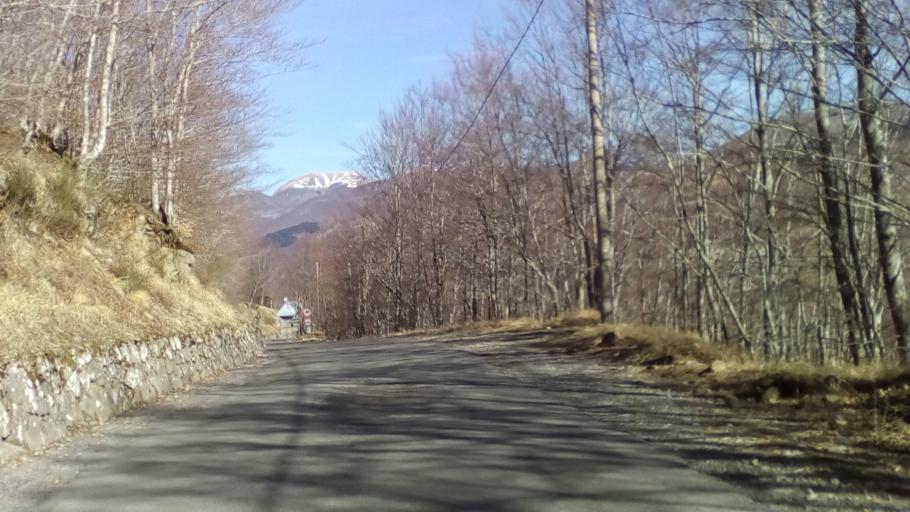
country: IT
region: Tuscany
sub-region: Provincia di Lucca
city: Castiglione di Garfagnana
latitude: 44.1756
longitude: 10.4615
